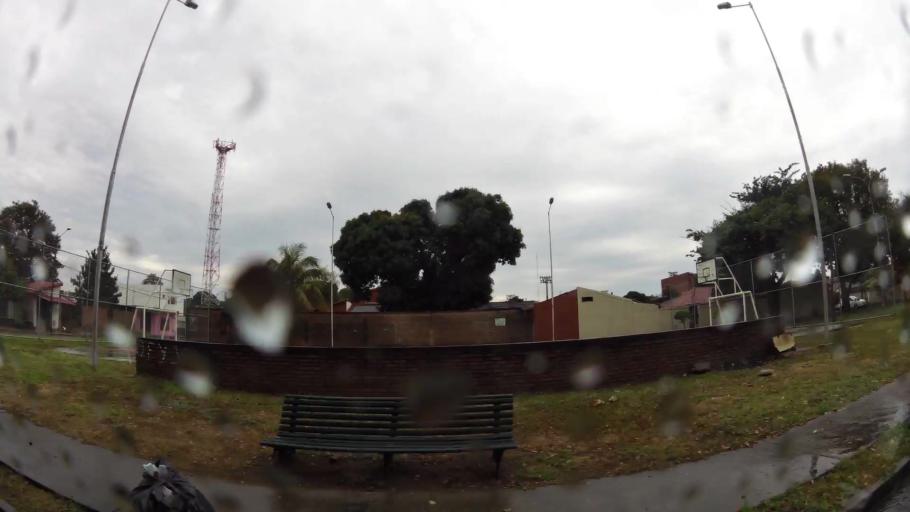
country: BO
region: Santa Cruz
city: Santa Cruz de la Sierra
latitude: -17.8081
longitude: -63.1656
